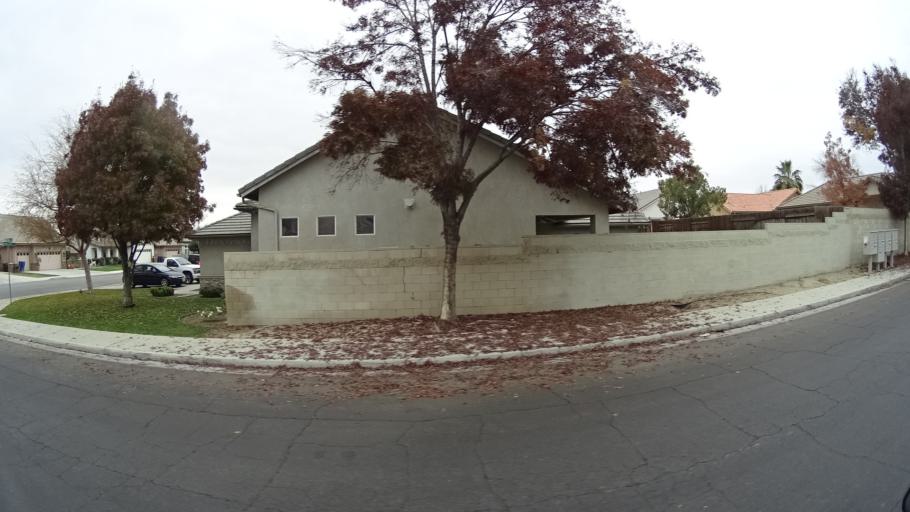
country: US
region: California
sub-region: Kern County
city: Greenfield
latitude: 35.2882
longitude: -119.0353
